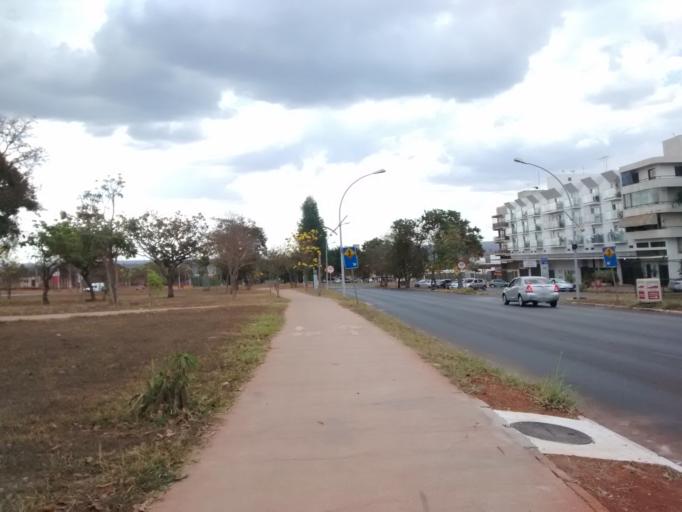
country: BR
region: Federal District
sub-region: Brasilia
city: Brasilia
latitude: -15.7402
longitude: -47.9017
